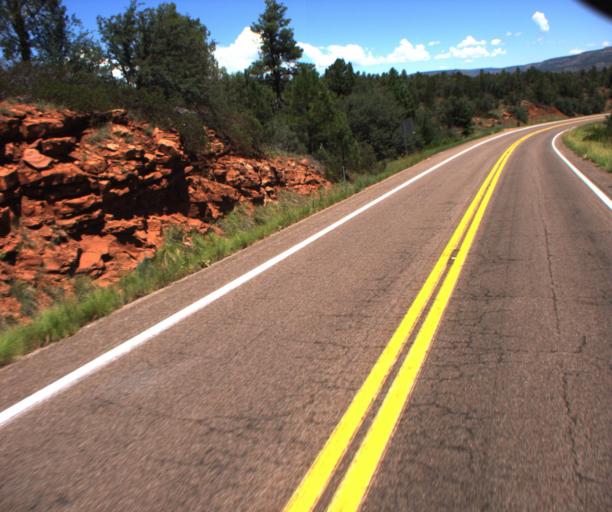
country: US
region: Arizona
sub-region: Navajo County
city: Cibecue
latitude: 33.9741
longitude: -110.3152
